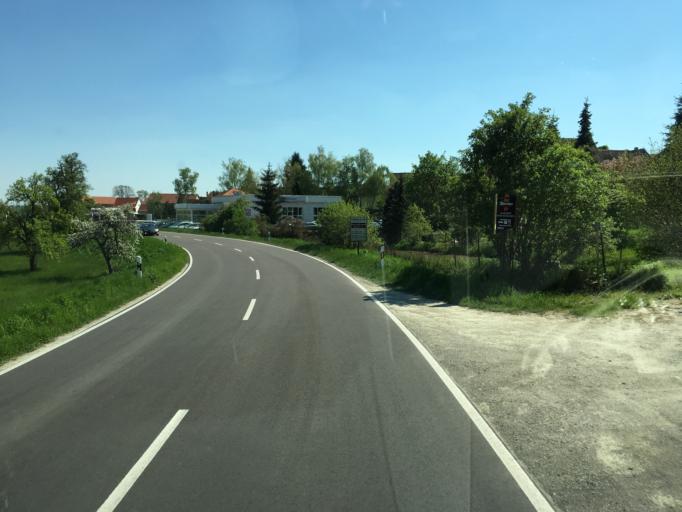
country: DE
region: Saxony-Anhalt
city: Freyburg
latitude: 51.1832
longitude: 11.7780
